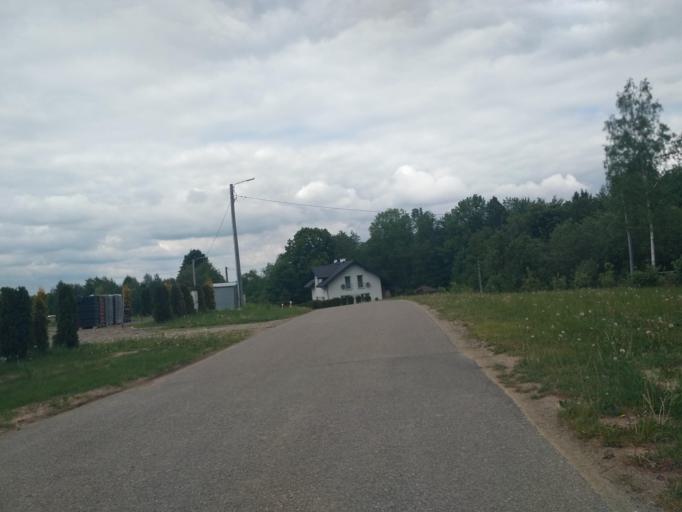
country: PL
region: Subcarpathian Voivodeship
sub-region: Powiat jasielski
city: Tarnowiec
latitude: 49.6966
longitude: 21.5810
